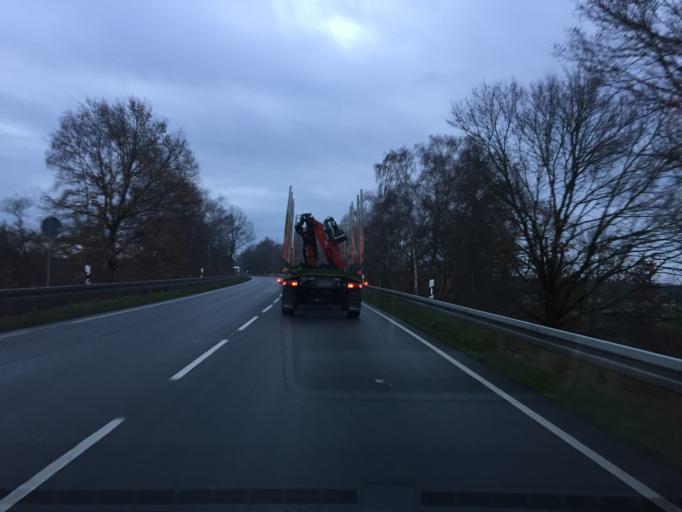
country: DE
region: Lower Saxony
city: Kirchdorf
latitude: 52.5934
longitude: 8.8313
